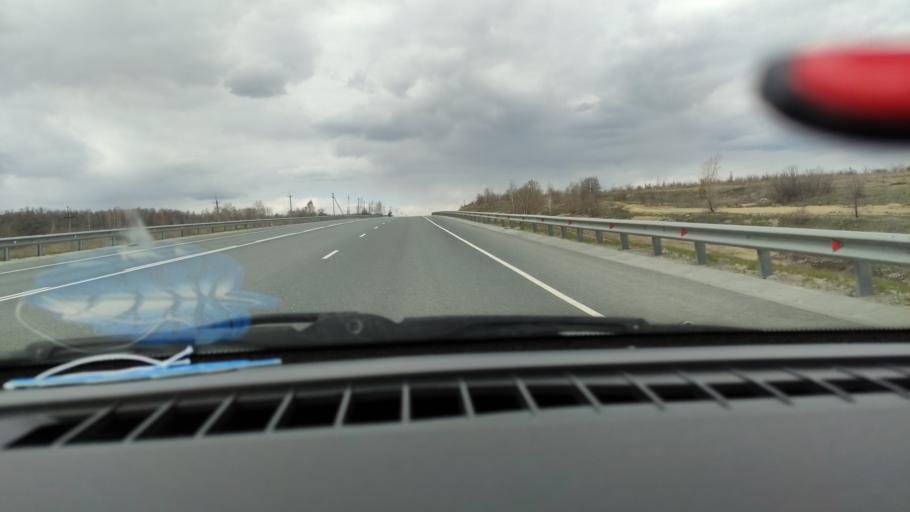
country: RU
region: Saratov
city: Shikhany
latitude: 52.1442
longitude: 47.2010
